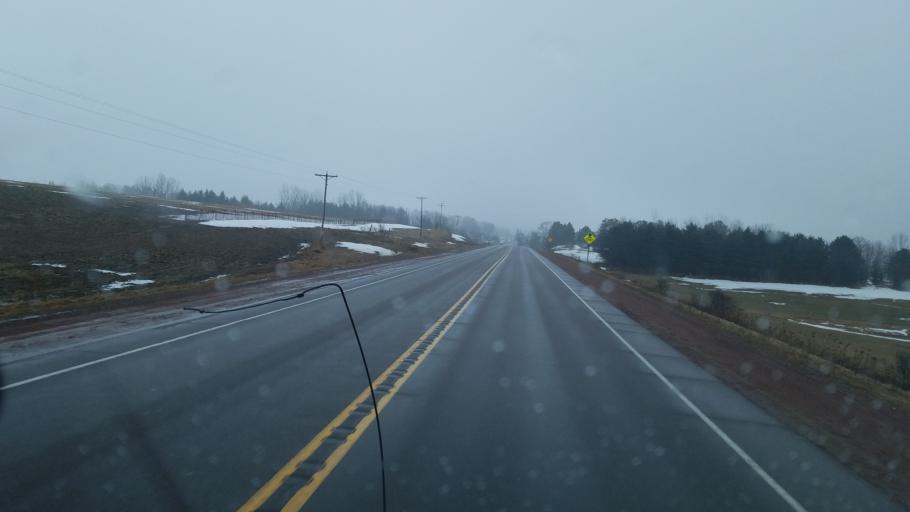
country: US
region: Wisconsin
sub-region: Wood County
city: Marshfield
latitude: 44.5988
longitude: -90.2850
